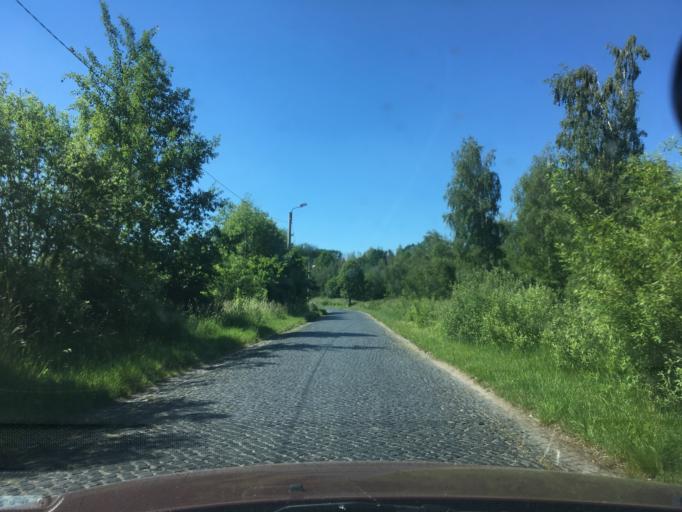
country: PL
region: Silesian Voivodeship
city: Zawidow
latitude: 51.0242
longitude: 15.0422
